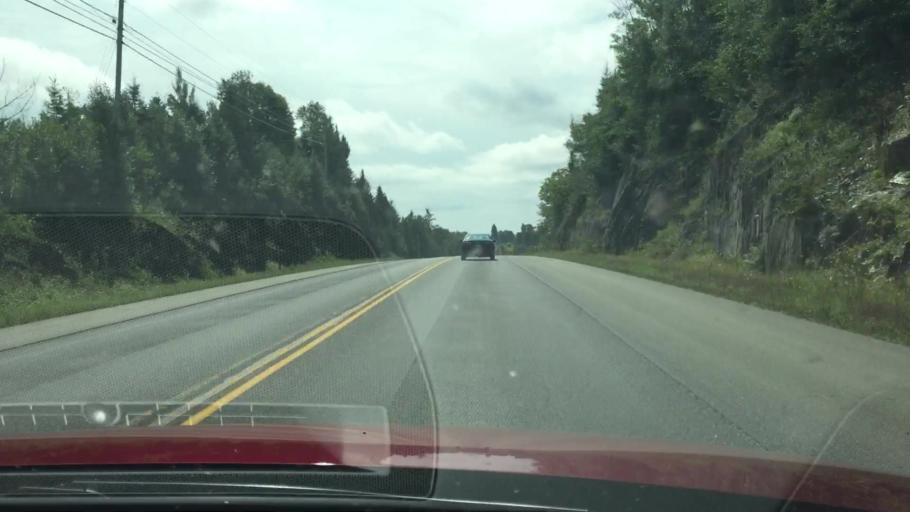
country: US
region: Maine
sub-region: Aroostook County
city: Houlton
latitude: 46.3526
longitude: -67.8422
